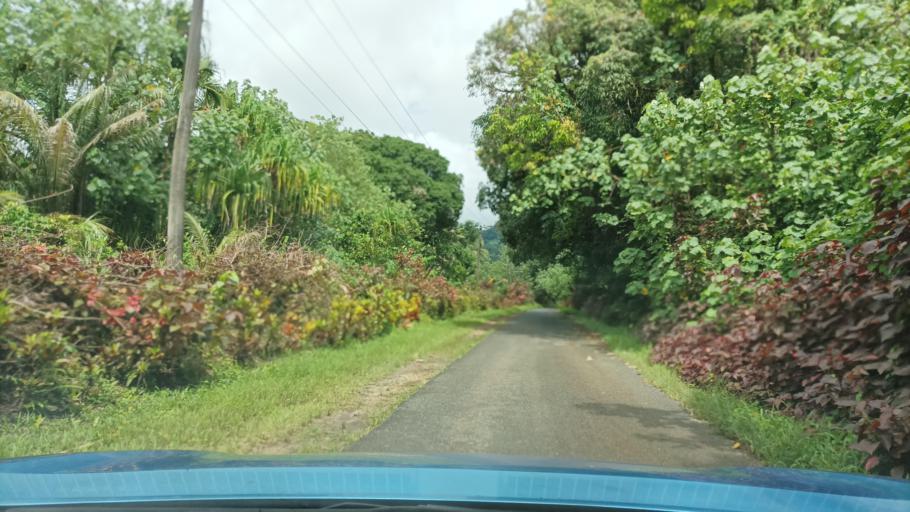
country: FM
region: Pohnpei
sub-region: Madolenihm Municipality
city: Madolenihm Municipality Government
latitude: 6.8881
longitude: 158.3152
